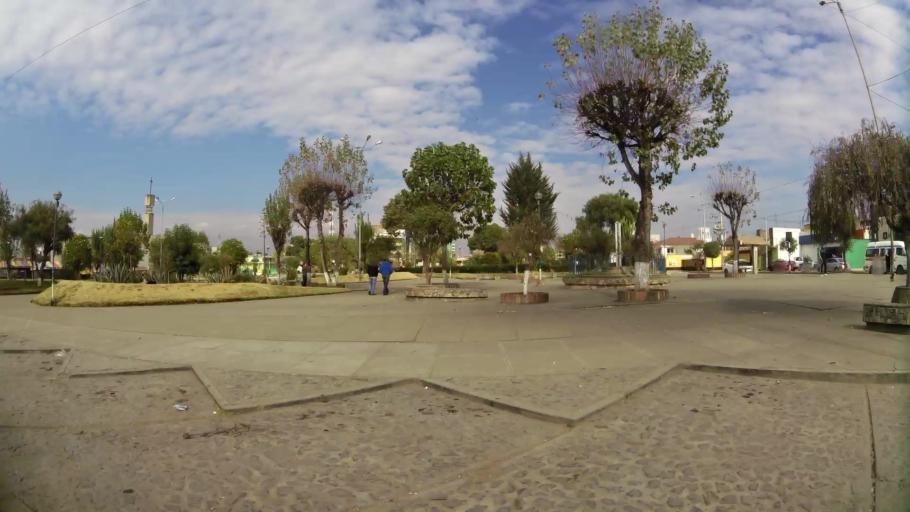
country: PE
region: Junin
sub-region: Provincia de Huancayo
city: Huancayo
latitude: -12.0597
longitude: -75.2033
